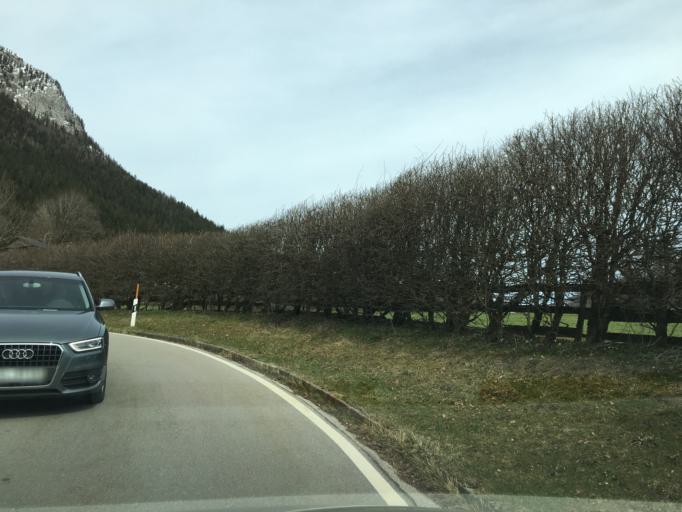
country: DE
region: Bavaria
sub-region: Upper Bavaria
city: Ramsau
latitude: 47.6115
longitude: 12.8608
